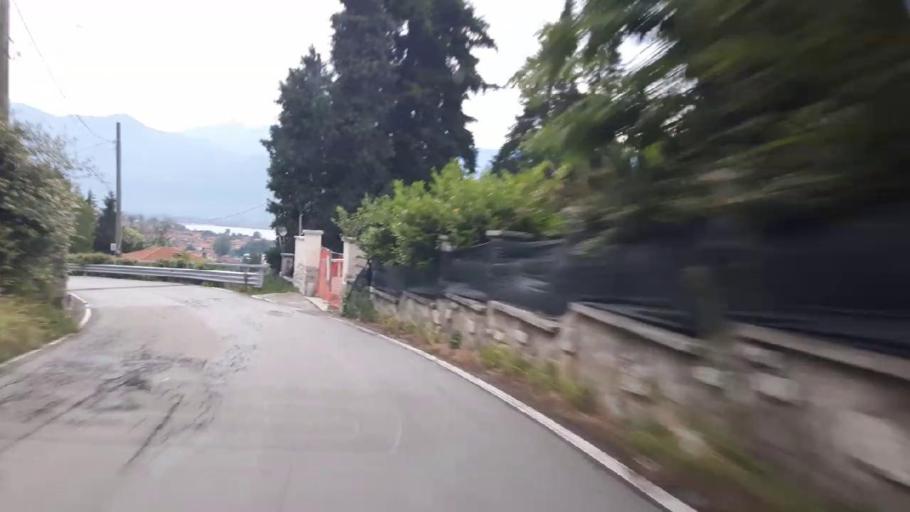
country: IT
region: Piedmont
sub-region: Provincia Verbano-Cusio-Ossola
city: Baveno
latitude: 45.9028
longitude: 8.5023
